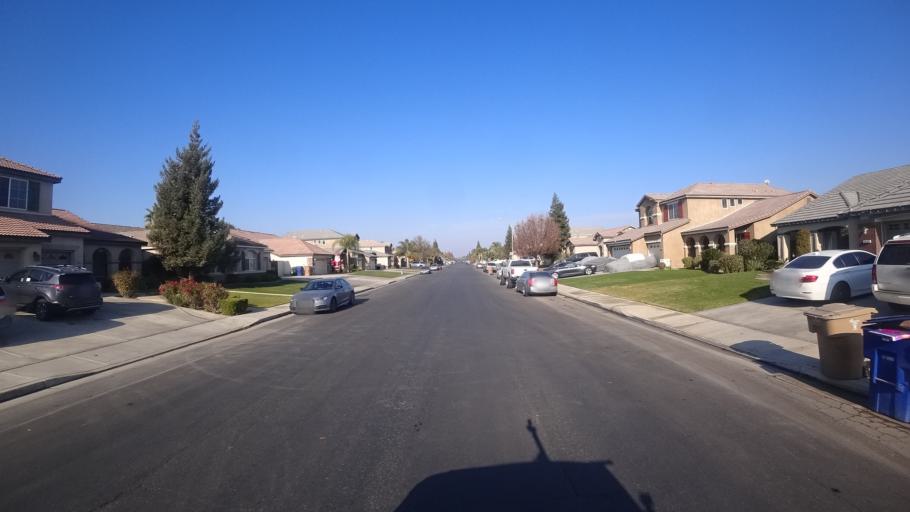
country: US
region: California
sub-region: Kern County
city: Greenacres
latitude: 35.3062
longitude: -119.1202
